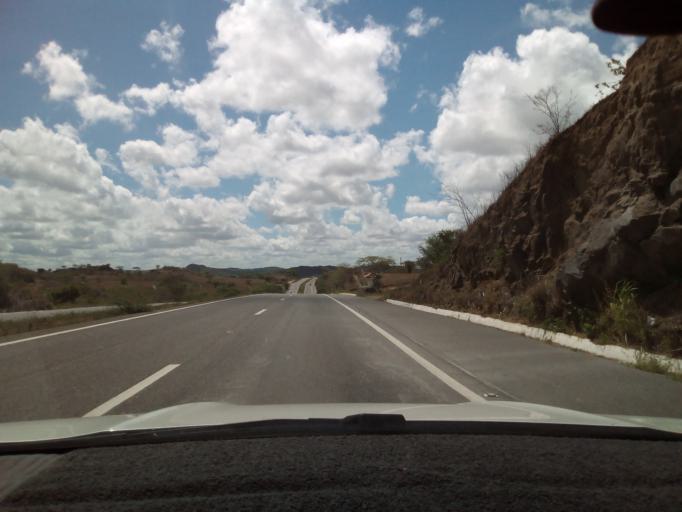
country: BR
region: Paraiba
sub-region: Campina Grande
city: Campina Grande
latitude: -7.2558
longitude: -35.8227
